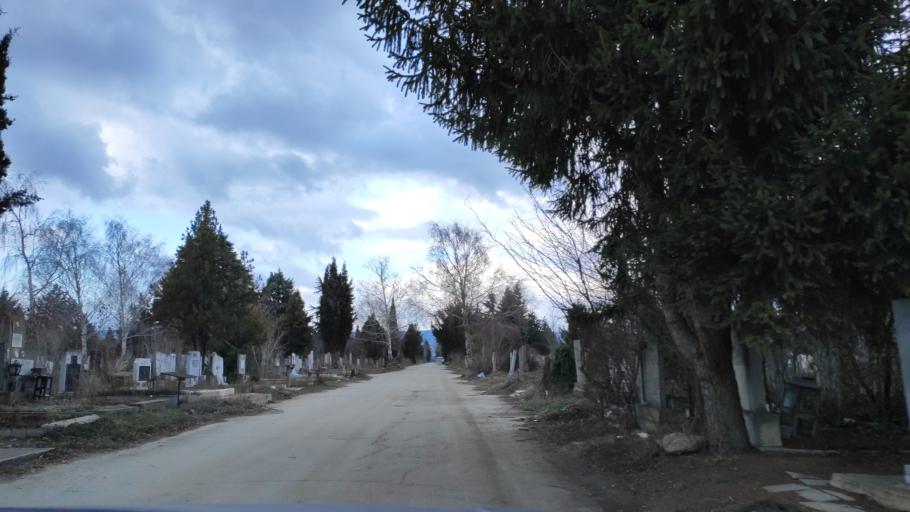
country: BG
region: Varna
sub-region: Obshtina Aksakovo
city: Aksakovo
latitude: 43.2192
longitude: 27.8090
